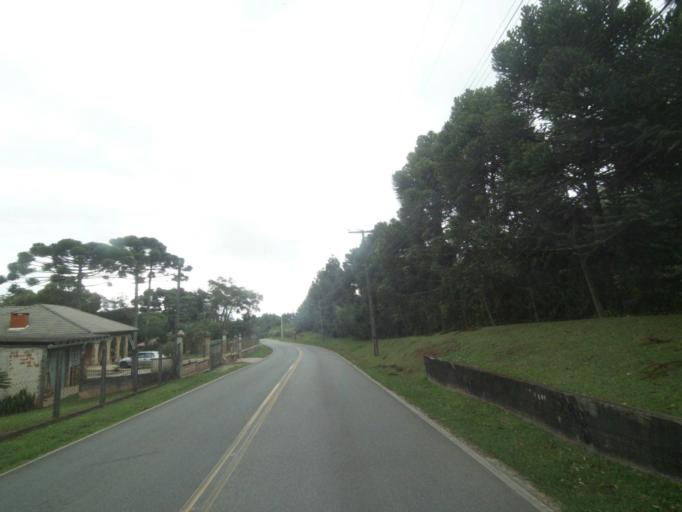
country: BR
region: Parana
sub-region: Quatro Barras
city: Quatro Barras
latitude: -25.3534
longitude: -49.1214
